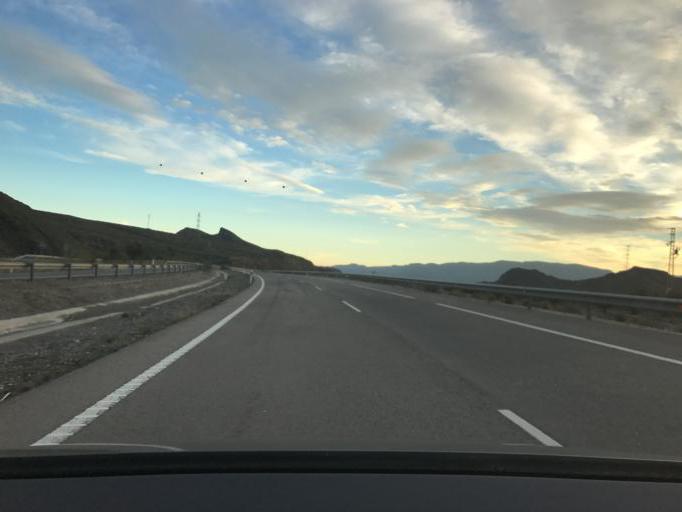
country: ES
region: Andalusia
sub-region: Provincia de Almeria
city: Rioja
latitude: 36.9886
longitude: -2.4637
